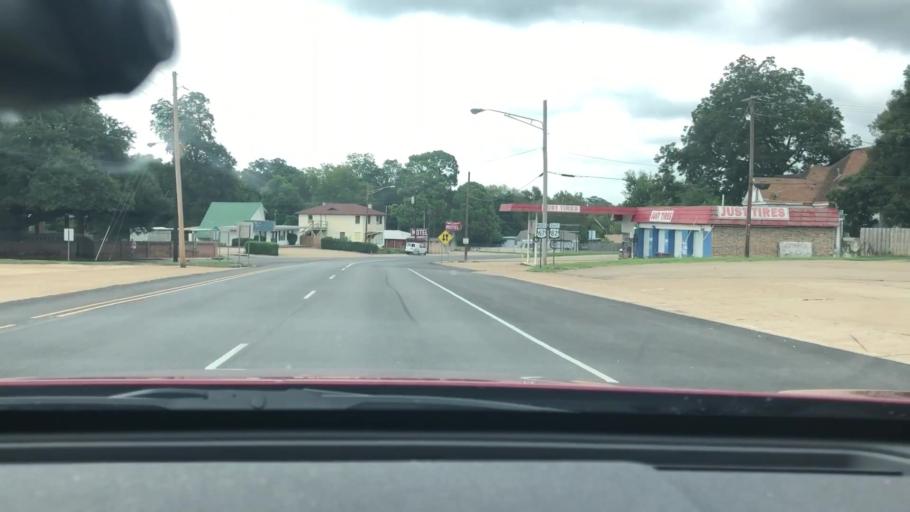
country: US
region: Arkansas
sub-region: Miller County
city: Texarkana
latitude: 33.4305
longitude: -94.0360
